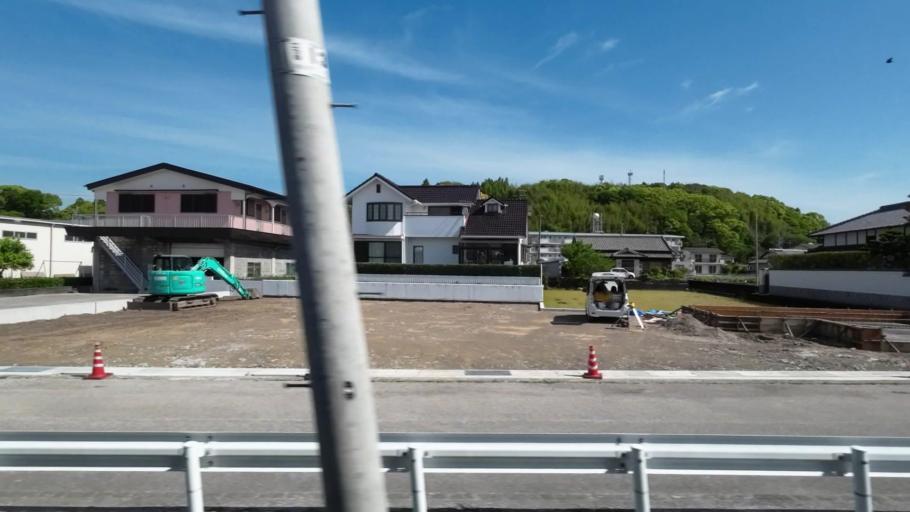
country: JP
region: Kochi
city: Kochi-shi
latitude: 33.5783
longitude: 133.6343
